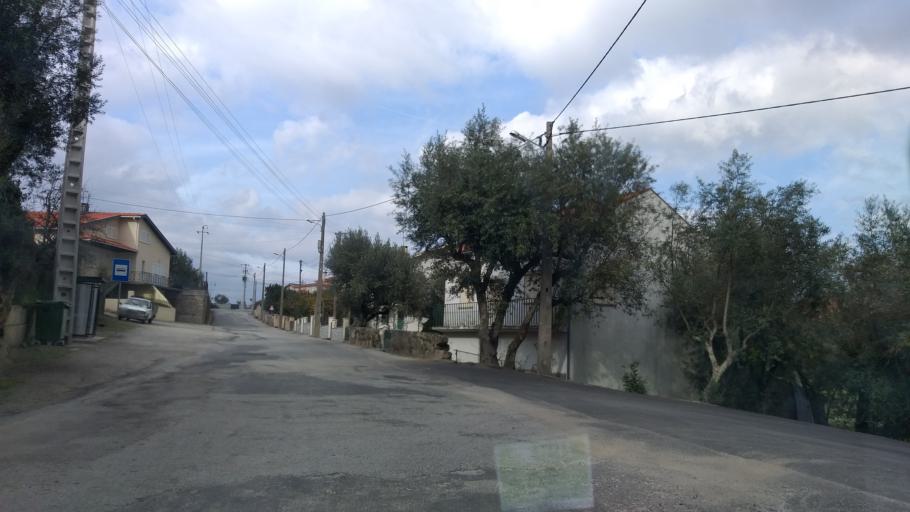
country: PT
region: Guarda
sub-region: Seia
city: Seia
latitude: 40.4667
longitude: -7.6874
